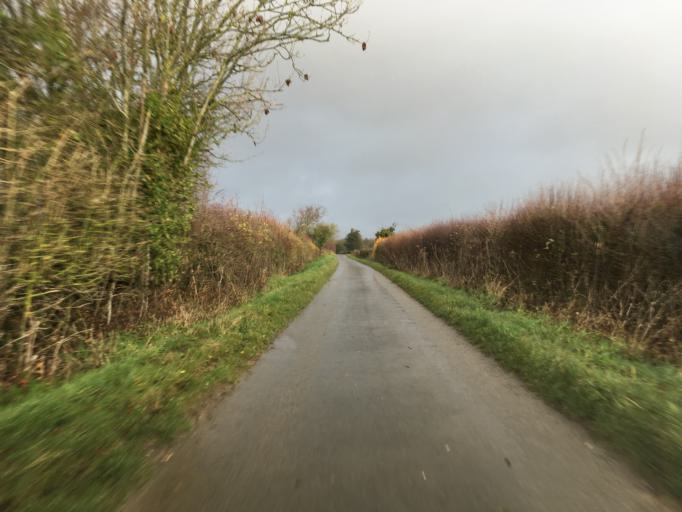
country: GB
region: England
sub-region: Wiltshire
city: Hankerton
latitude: 51.6472
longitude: -2.0723
